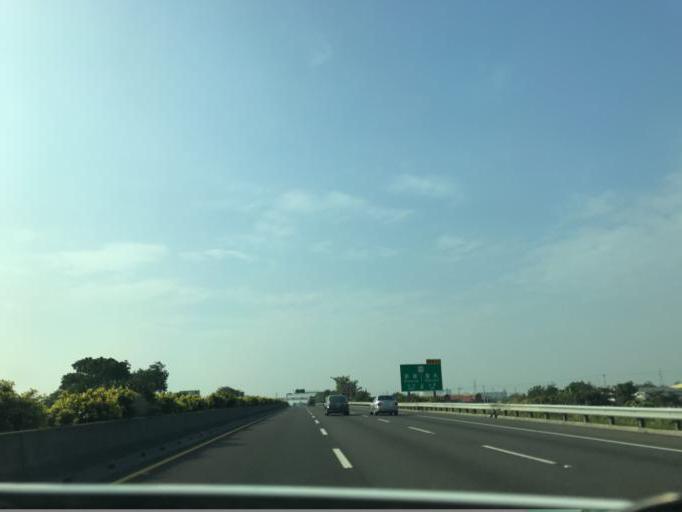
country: TW
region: Taiwan
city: Xinying
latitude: 23.3255
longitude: 120.3010
